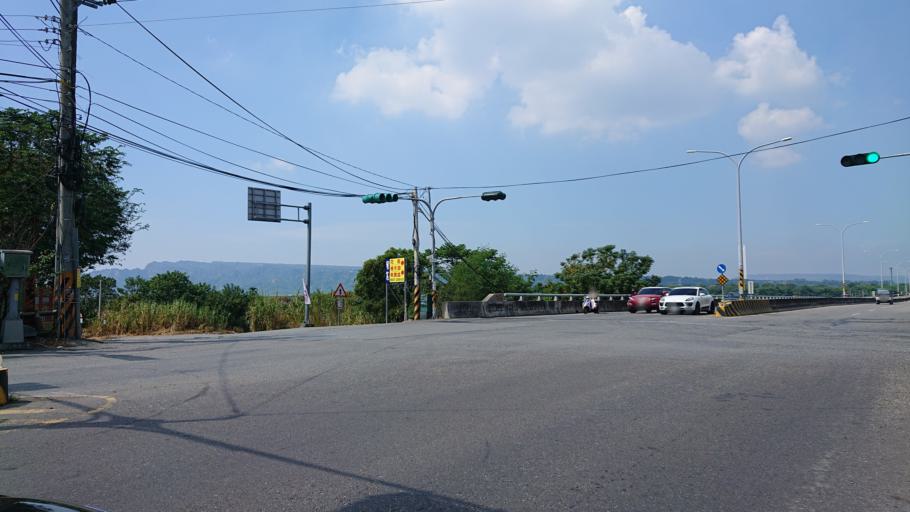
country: TW
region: Taiwan
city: Lugu
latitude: 23.8127
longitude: 120.7092
